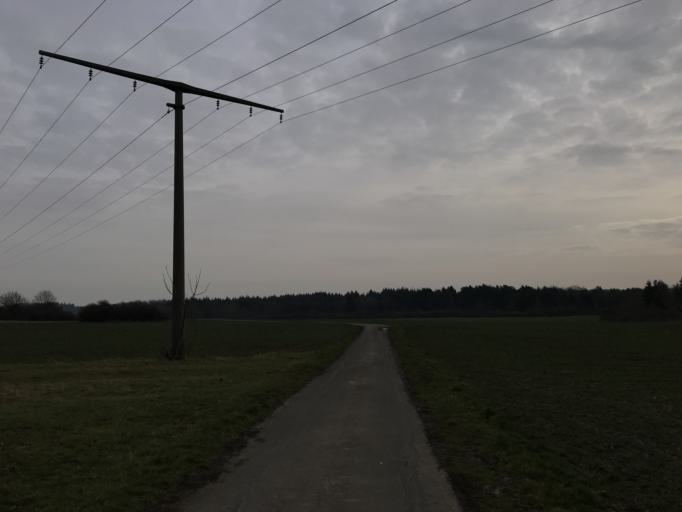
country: DE
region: Hesse
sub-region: Regierungsbezirk Giessen
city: Alten Buseck
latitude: 50.5931
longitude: 8.7545
